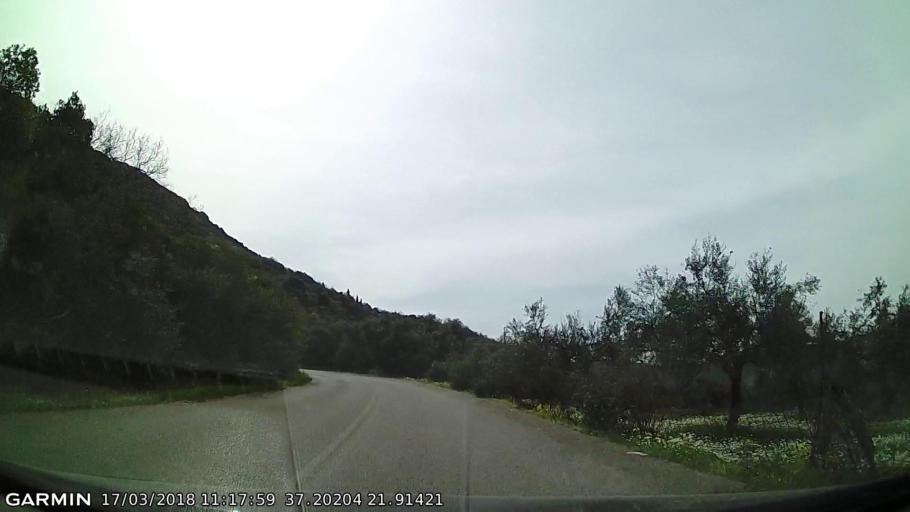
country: GR
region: Peloponnese
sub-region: Nomos Messinias
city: Meligalas
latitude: 37.2020
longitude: 21.9141
